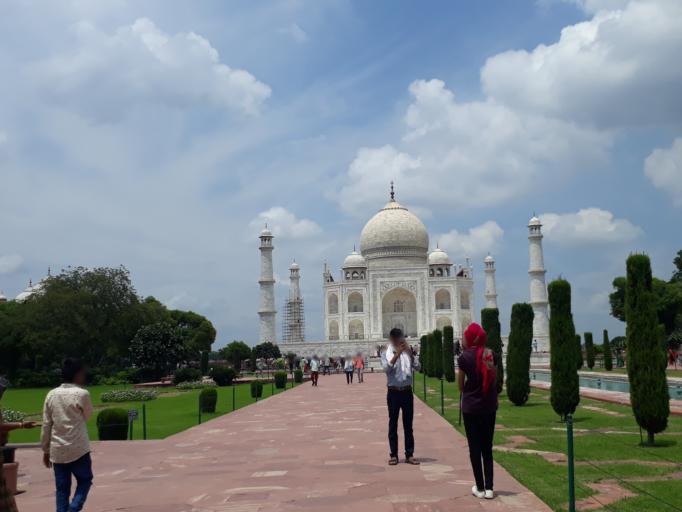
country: IN
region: Uttar Pradesh
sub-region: Agra
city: Agra
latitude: 27.1724
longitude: 78.0420
